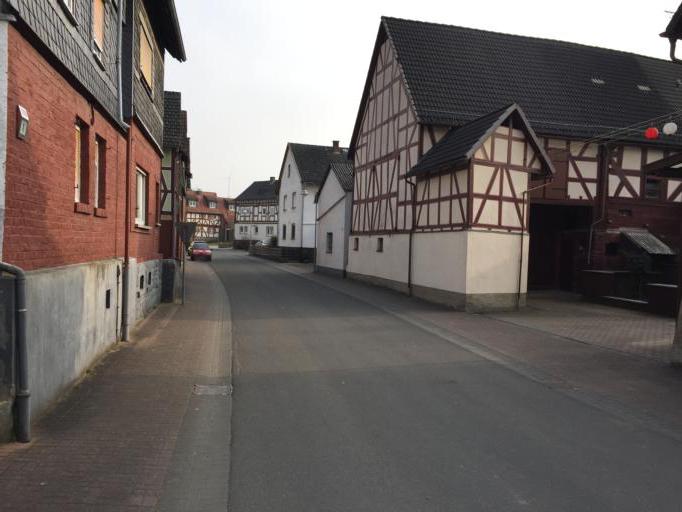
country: DE
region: Hesse
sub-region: Regierungsbezirk Giessen
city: Bischoffen
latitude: 50.6607
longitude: 8.4899
